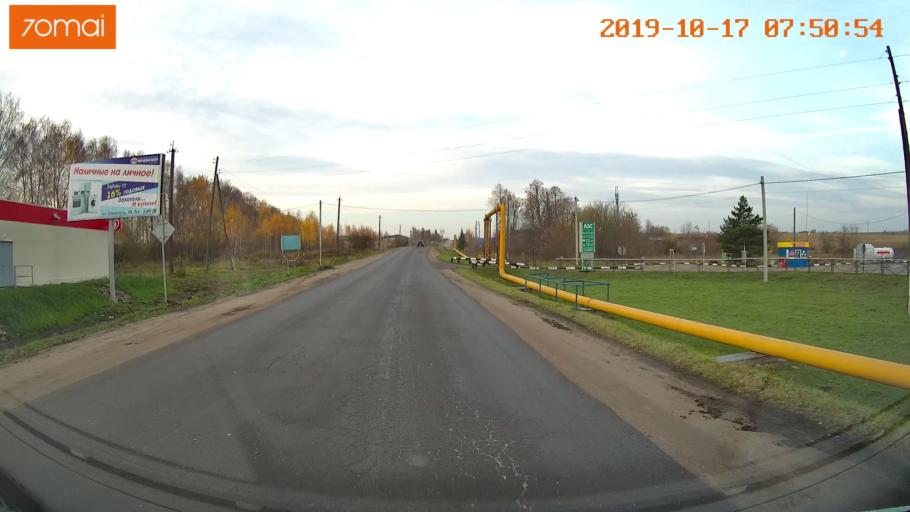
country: RU
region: Vladimir
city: Yur'yev-Pol'skiy
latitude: 56.4837
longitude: 39.6597
